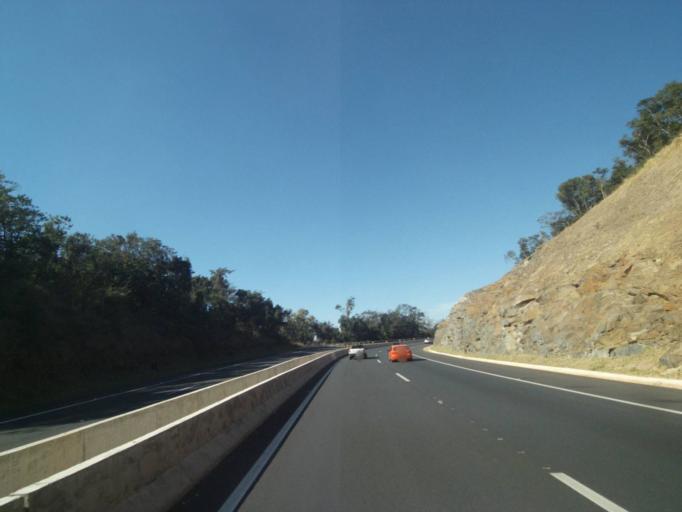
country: BR
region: Parana
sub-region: Tibagi
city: Tibagi
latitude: -24.7905
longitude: -50.5024
